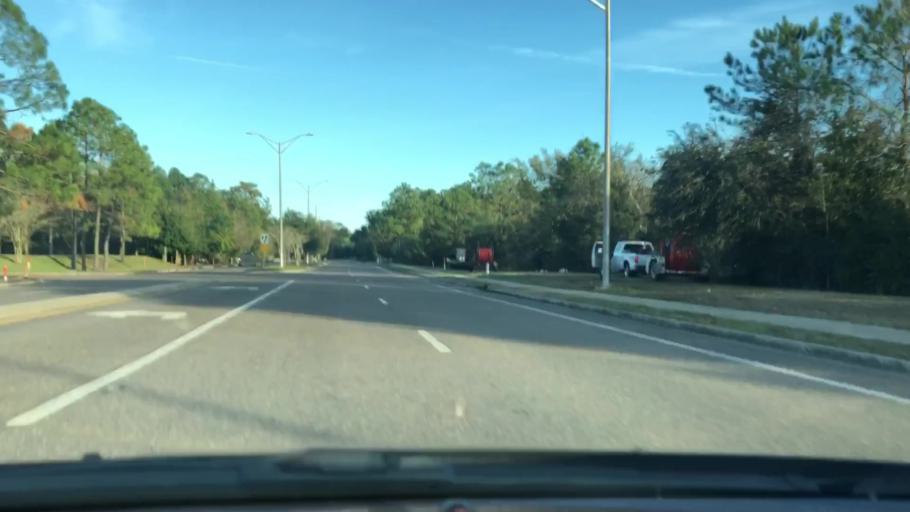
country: US
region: Florida
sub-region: Duval County
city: Jacksonville
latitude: 30.2489
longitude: -81.5771
